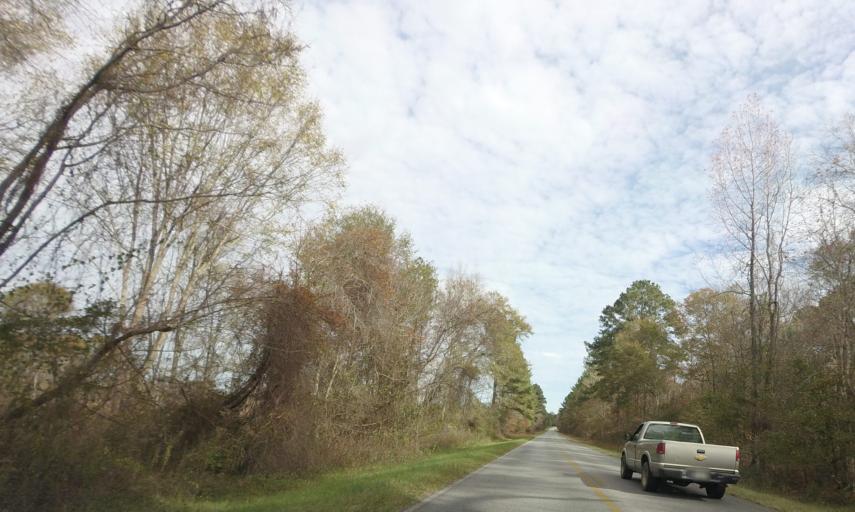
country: US
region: Georgia
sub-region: Dodge County
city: Chester
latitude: 32.4536
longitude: -83.1413
